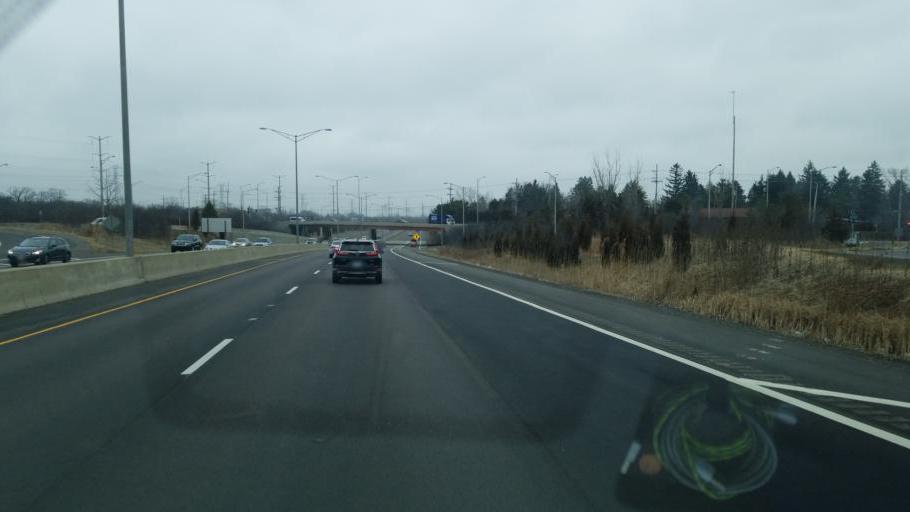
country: US
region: Illinois
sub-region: Lake County
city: Highland Park
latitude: 42.1582
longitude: -87.8041
